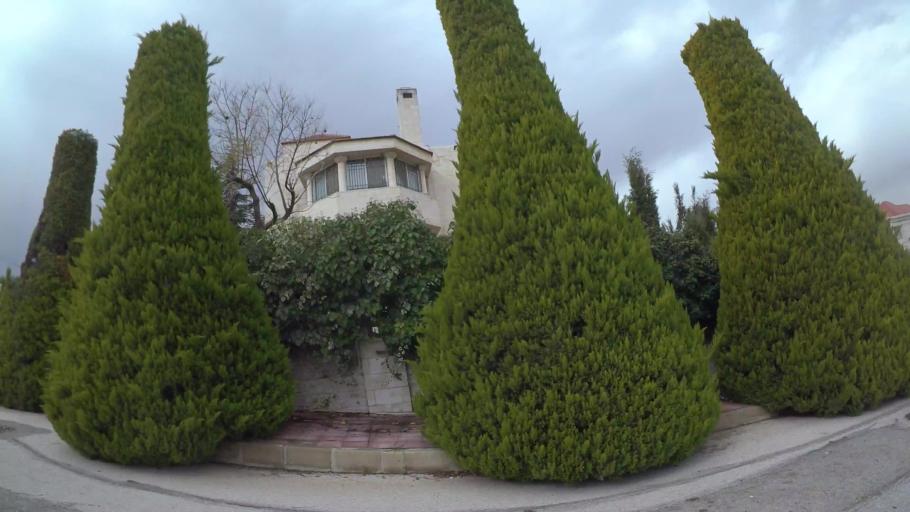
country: JO
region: Amman
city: Wadi as Sir
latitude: 31.9898
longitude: 35.8235
